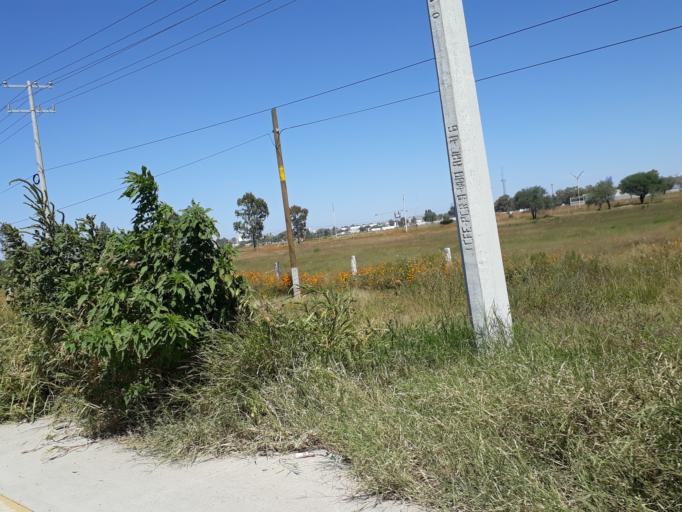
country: MX
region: Aguascalientes
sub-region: Aguascalientes
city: San Sebastian [Fraccionamiento]
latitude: 21.8190
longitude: -102.2937
